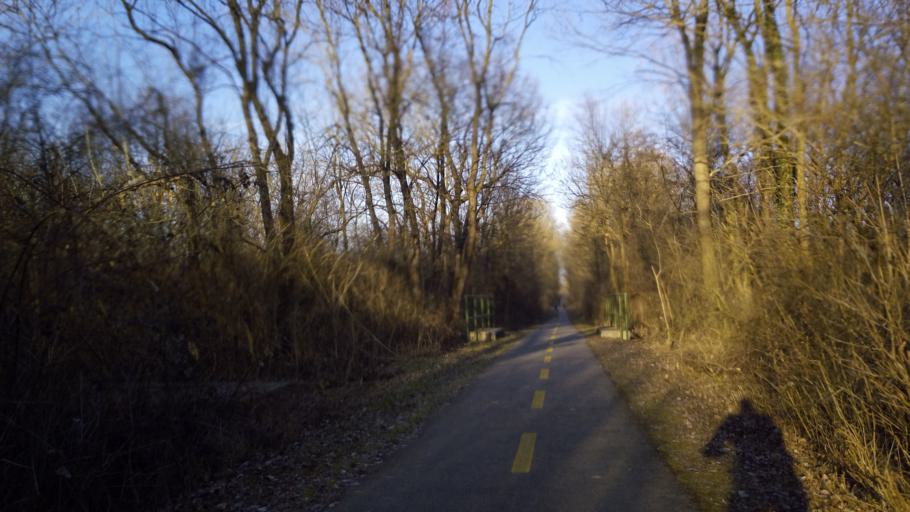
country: HU
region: Baranya
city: Pellerd
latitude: 46.0391
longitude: 18.1752
